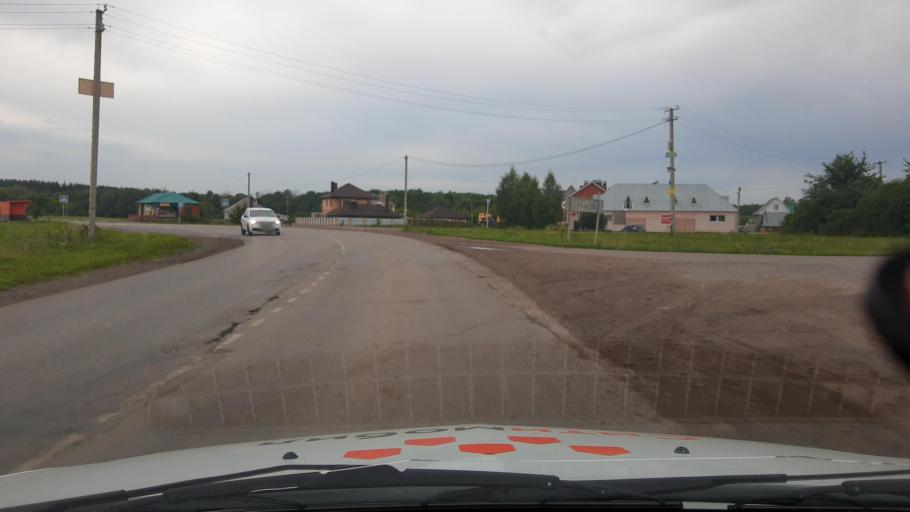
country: RU
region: Bashkortostan
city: Ufa
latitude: 54.5705
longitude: 55.9661
